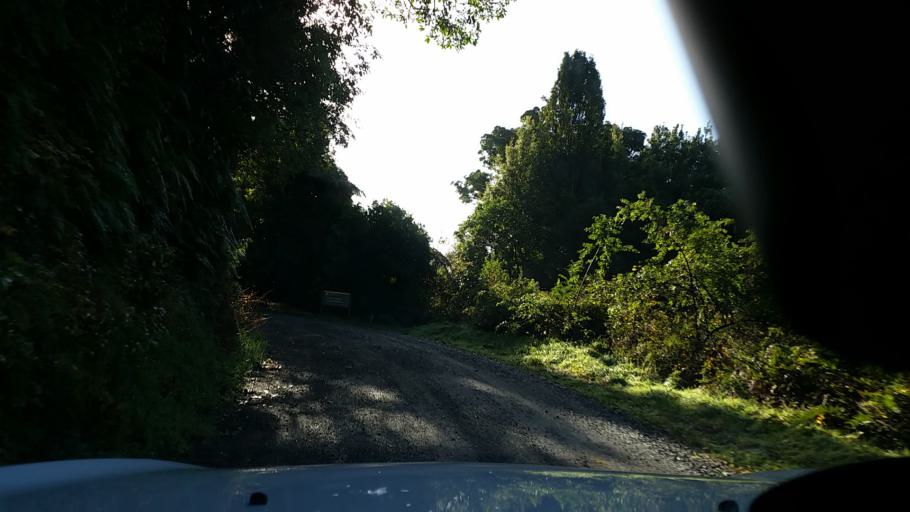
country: NZ
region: Bay of Plenty
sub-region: Kawerau District
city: Kawerau
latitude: -38.0298
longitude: 176.5566
